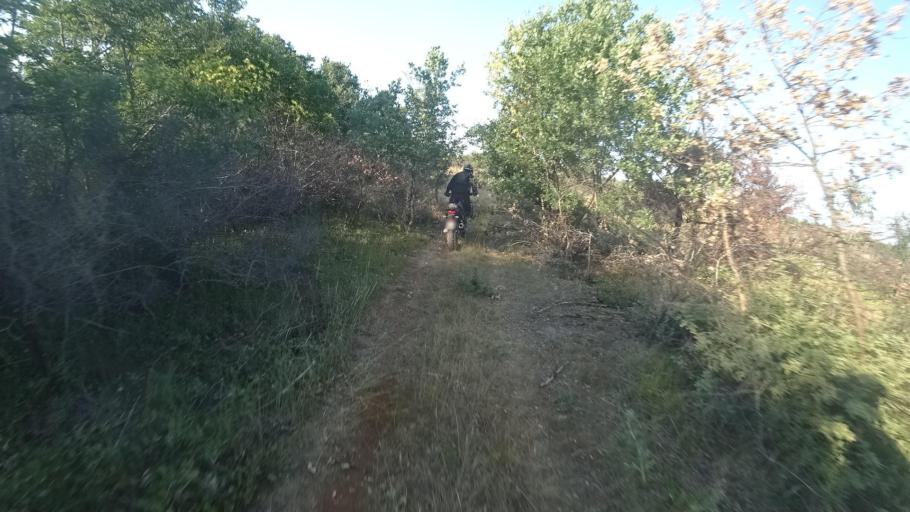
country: HR
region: Istarska
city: Galizana
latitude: 44.9504
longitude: 13.9056
